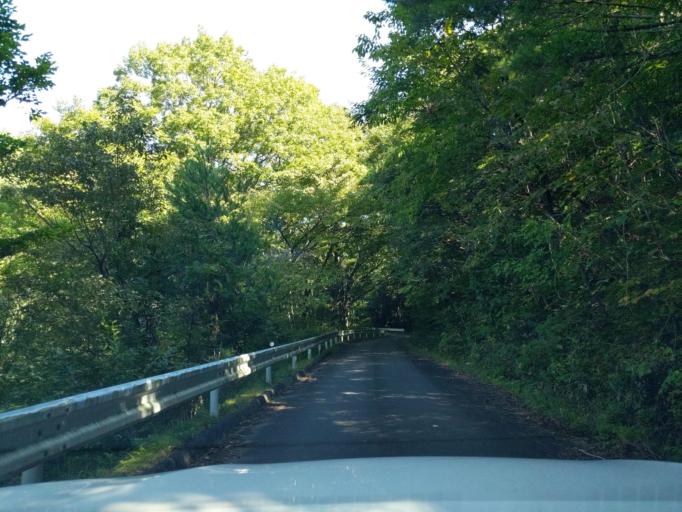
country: JP
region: Fukushima
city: Koriyama
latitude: 37.3986
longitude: 140.2380
